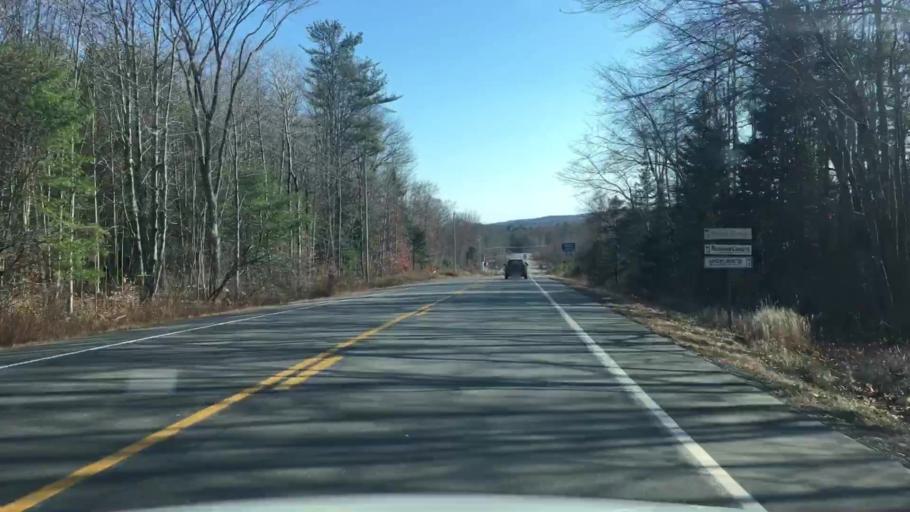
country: US
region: Maine
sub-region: Knox County
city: Washington
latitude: 44.2454
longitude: -69.3855
